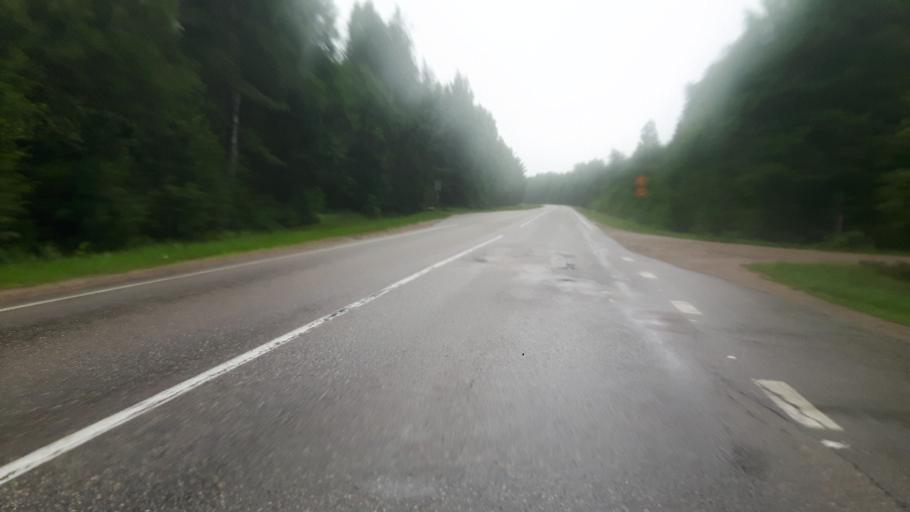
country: LV
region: Rucavas
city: Rucava
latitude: 56.1330
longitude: 21.1506
